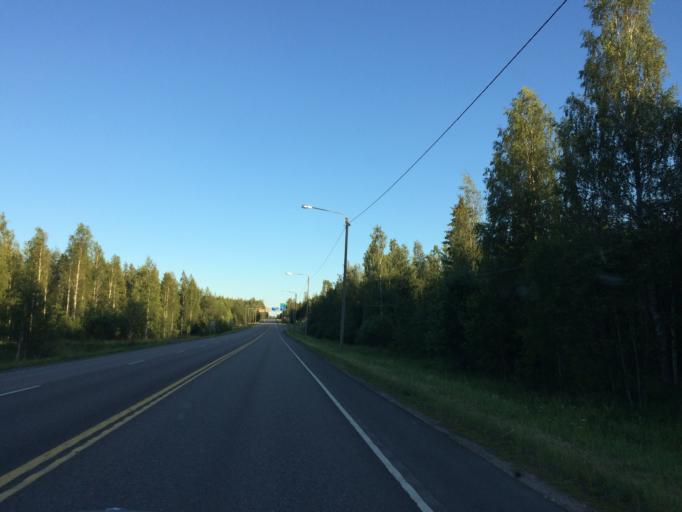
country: FI
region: Haeme
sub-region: Riihimaeki
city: Riihimaeki
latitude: 60.7537
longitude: 24.7215
